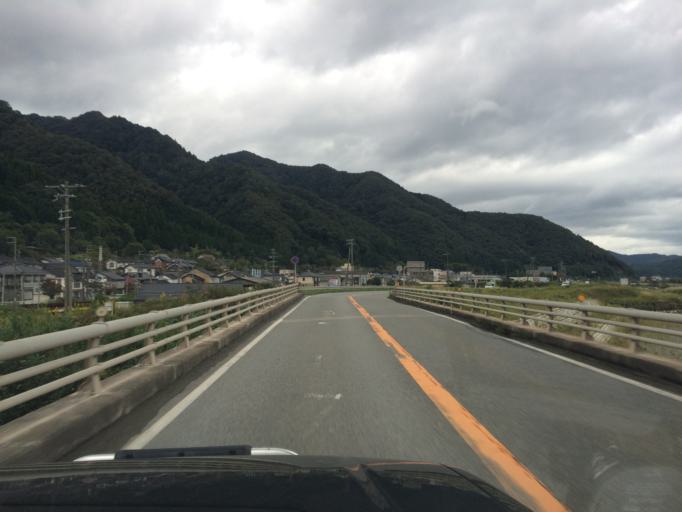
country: JP
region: Hyogo
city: Toyooka
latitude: 35.4095
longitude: 134.7786
